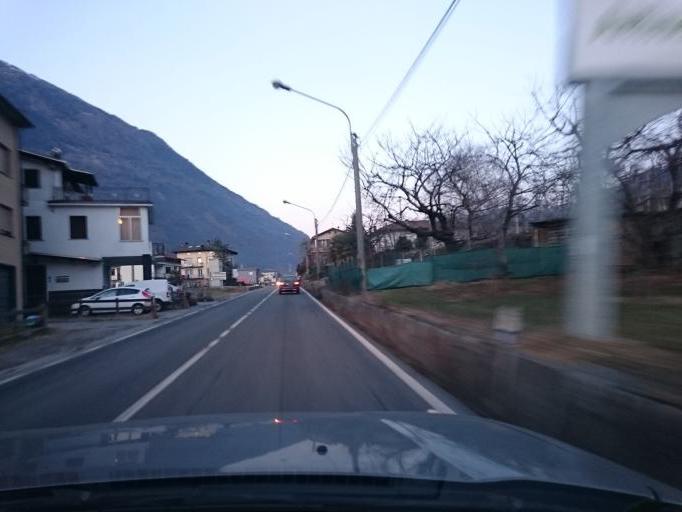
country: IT
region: Lombardy
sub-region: Provincia di Sondrio
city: Sernio
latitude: 46.2186
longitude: 10.1851
